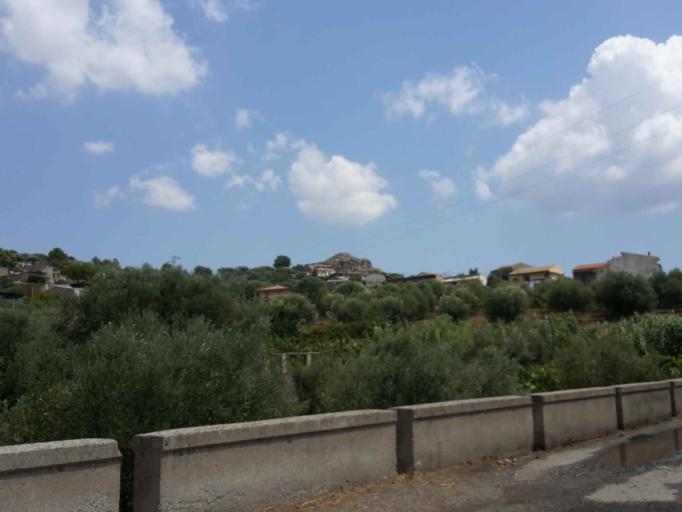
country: IT
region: Calabria
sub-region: Provincia di Reggio Calabria
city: Condofuri
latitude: 37.9862
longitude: 15.8437
